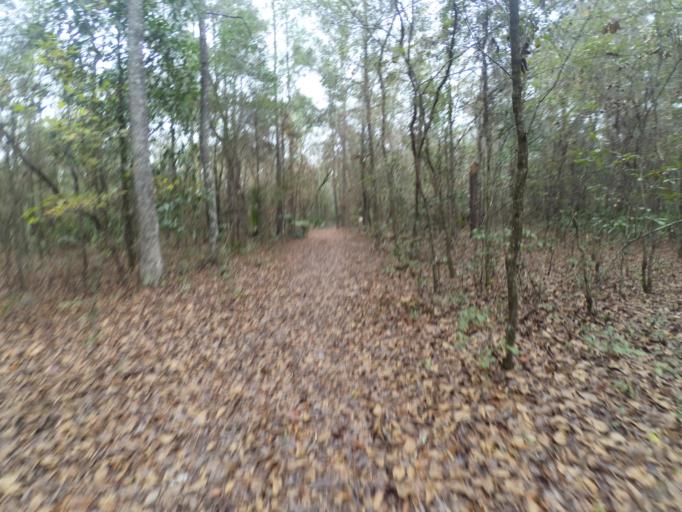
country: US
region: Florida
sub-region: Alachua County
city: Gainesville
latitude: 29.5424
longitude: -82.2729
